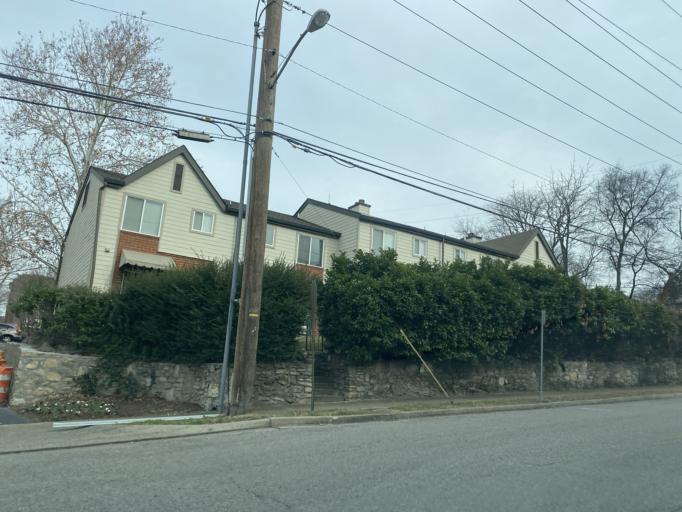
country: US
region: Tennessee
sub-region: Davidson County
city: Nashville
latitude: 36.1385
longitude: -86.7979
